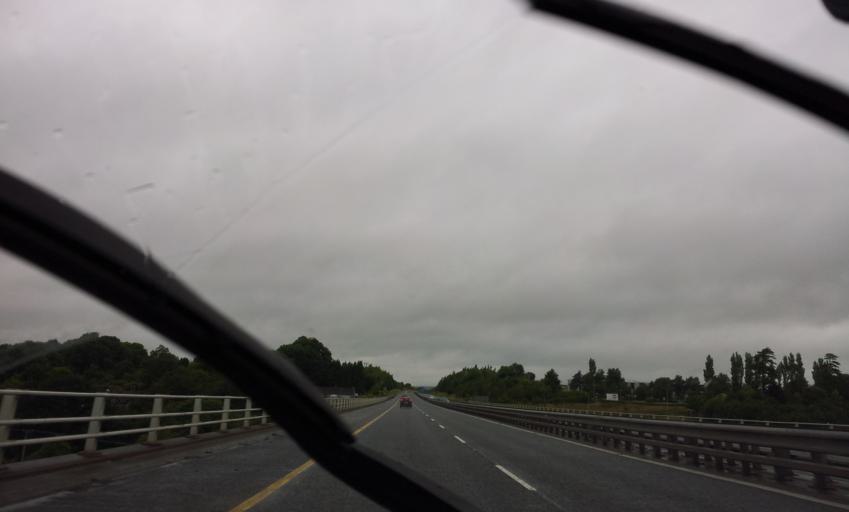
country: IE
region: Munster
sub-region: County Cork
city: Fermoy
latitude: 52.1395
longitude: -8.2623
